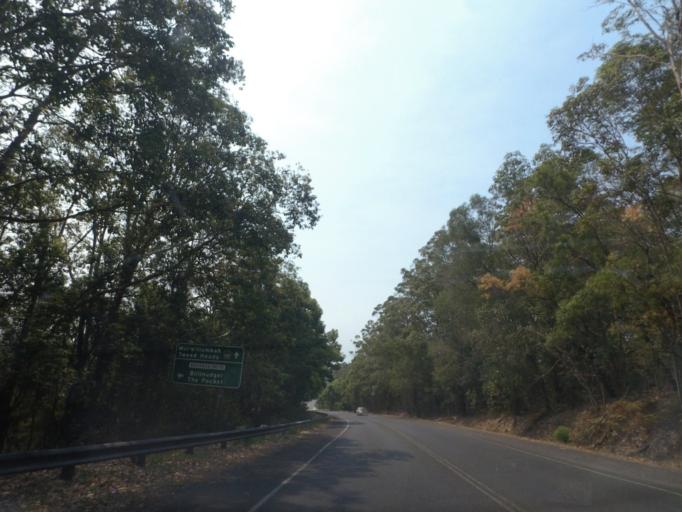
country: AU
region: New South Wales
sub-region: Byron Shire
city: Brunswick Heads
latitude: -28.5085
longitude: 153.5319
